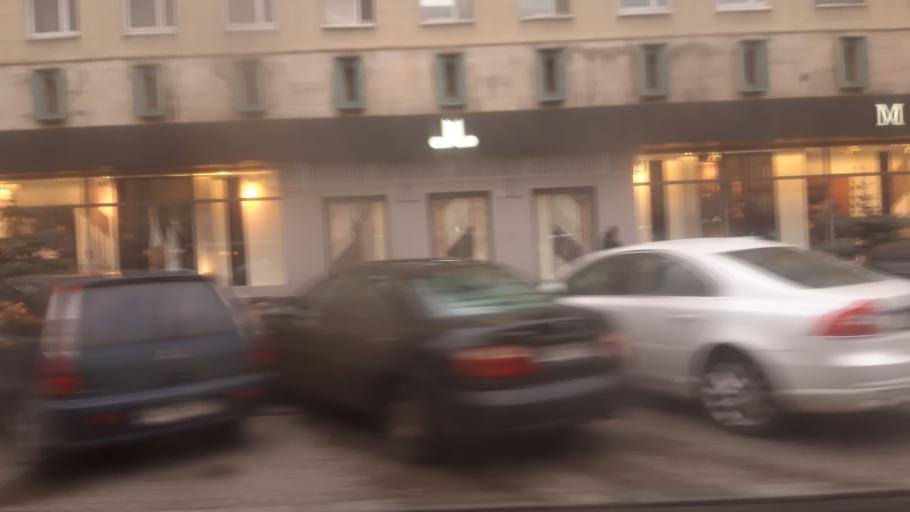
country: RU
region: St.-Petersburg
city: Kupchino
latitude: 59.8472
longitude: 30.3219
